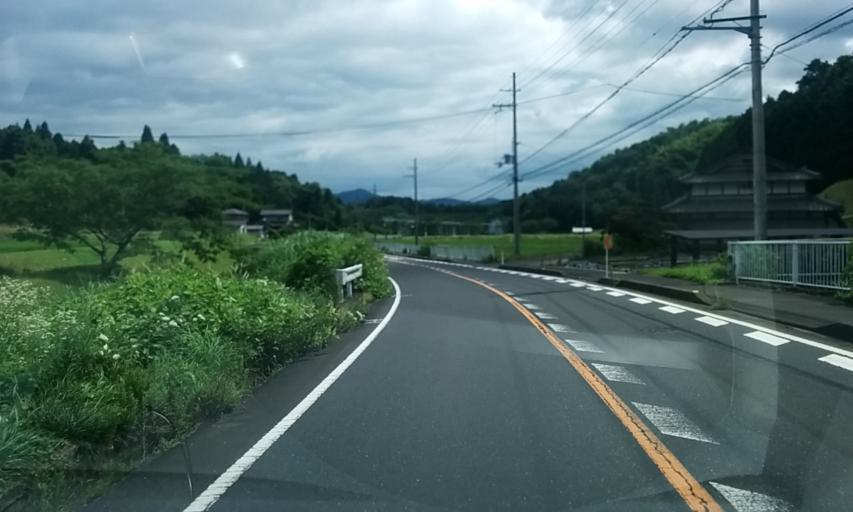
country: JP
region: Kyoto
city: Ayabe
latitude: 35.3355
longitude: 135.2685
